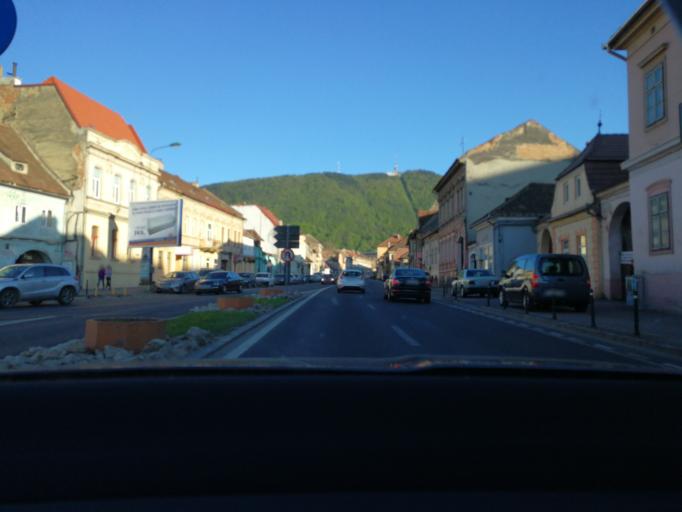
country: RO
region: Brasov
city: Brasov
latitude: 45.6505
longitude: 25.5872
